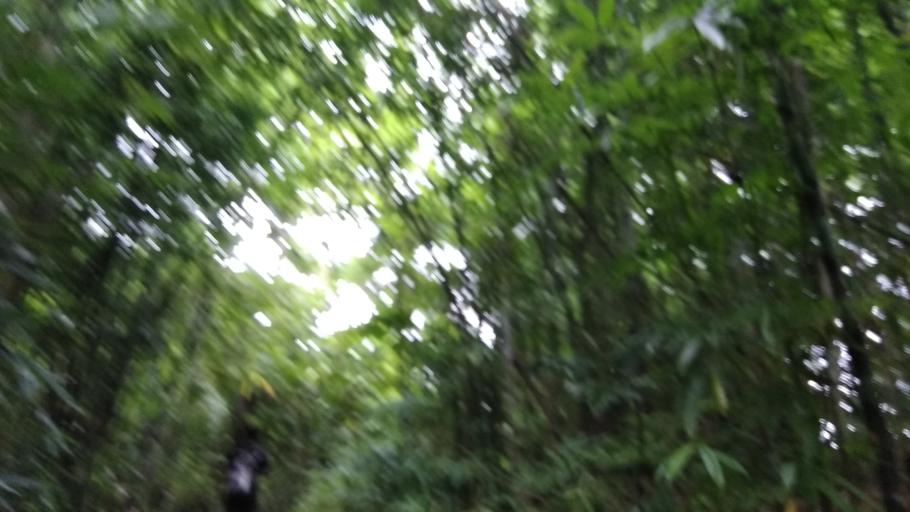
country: IN
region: Tripura
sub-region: Dhalai
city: Kamalpur
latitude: 24.1695
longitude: 91.8996
